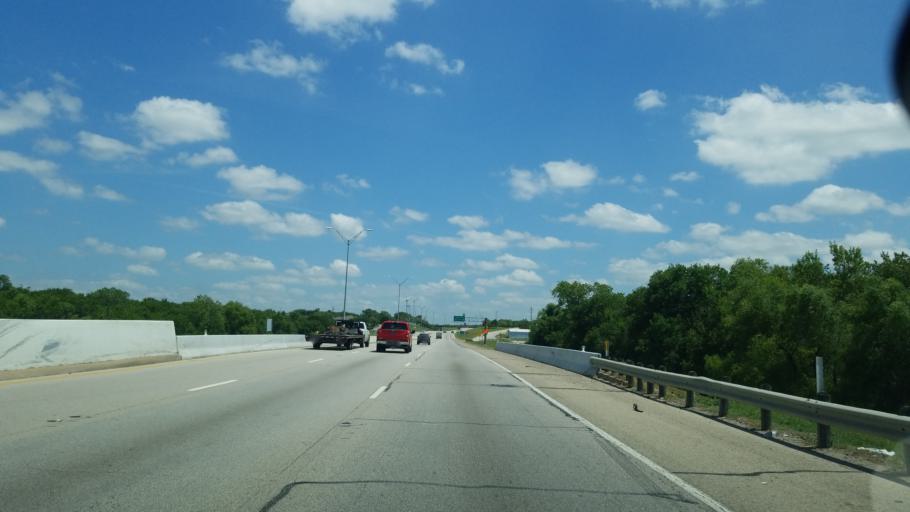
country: US
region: Texas
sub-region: Dallas County
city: Hutchins
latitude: 32.7384
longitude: -96.7180
